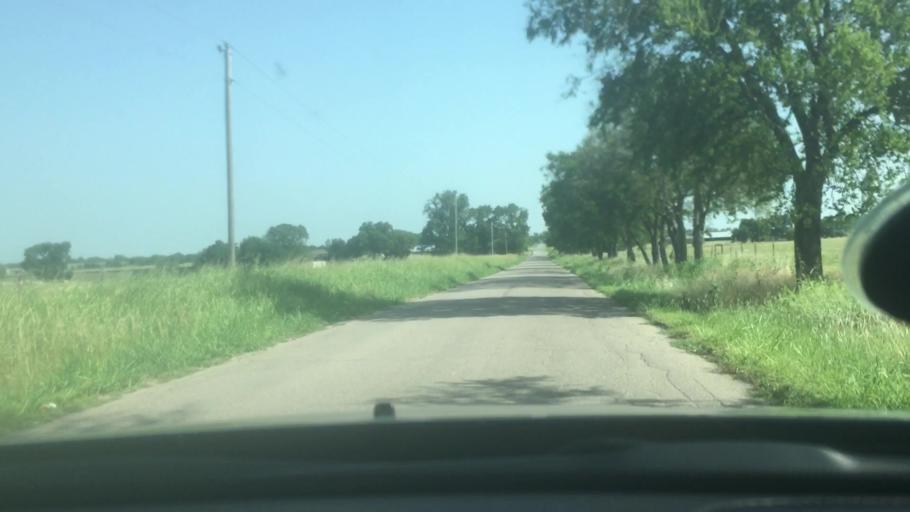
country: US
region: Oklahoma
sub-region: Bryan County
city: Calera
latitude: 33.9794
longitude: -96.4656
